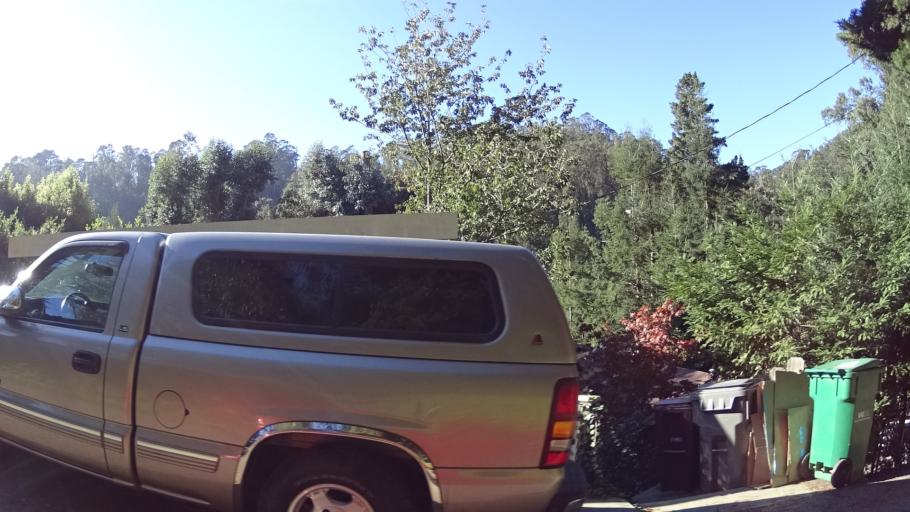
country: US
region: California
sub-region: Alameda County
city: Piedmont
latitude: 37.8450
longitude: -122.2077
